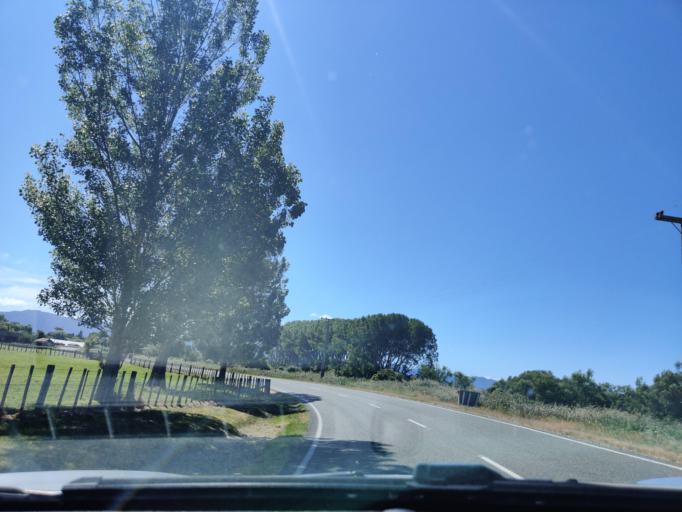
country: NZ
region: Wellington
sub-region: Upper Hutt City
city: Upper Hutt
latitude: -41.2893
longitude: 175.2714
